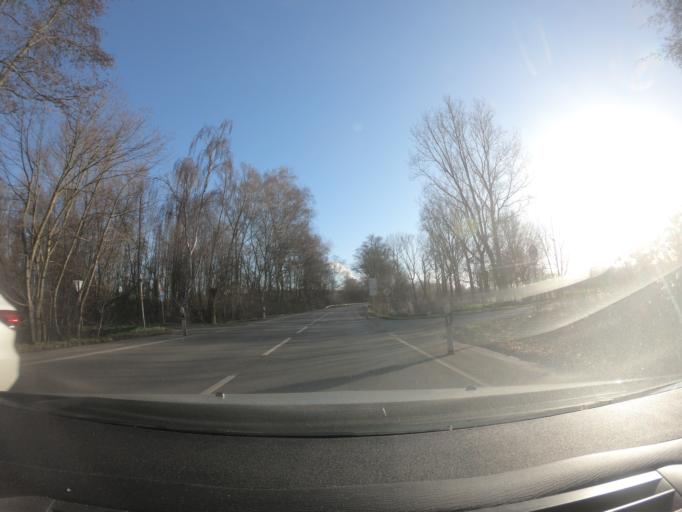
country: DE
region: North Rhine-Westphalia
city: Waltrop
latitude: 51.6259
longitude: 7.4473
